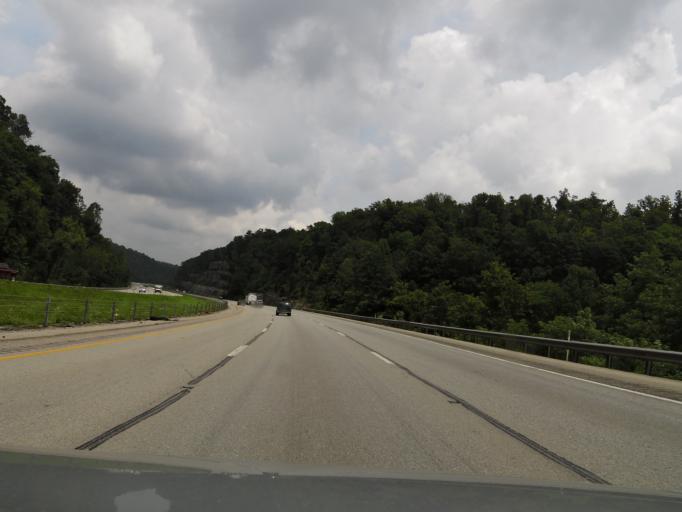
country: US
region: Kentucky
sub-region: Hardin County
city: Elizabethtown
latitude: 37.7456
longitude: -85.7938
